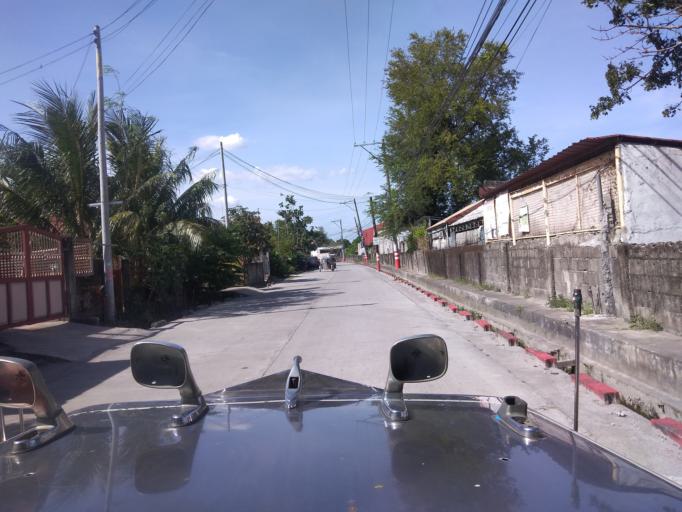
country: PH
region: Central Luzon
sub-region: Province of Pampanga
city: Magliman
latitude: 15.0326
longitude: 120.6669
